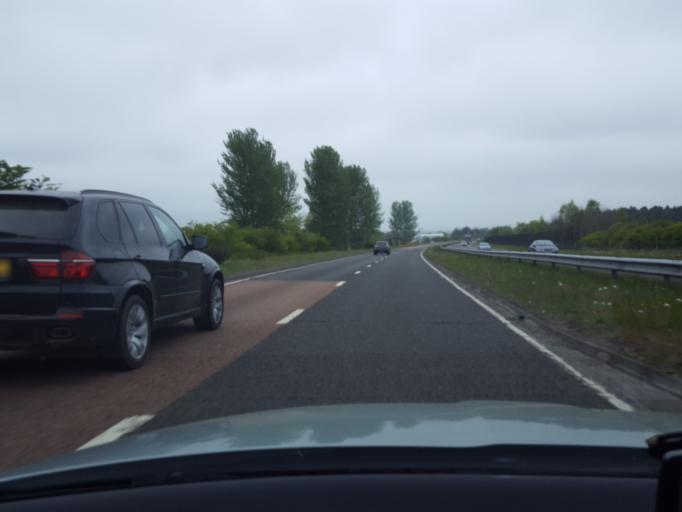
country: GB
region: Scotland
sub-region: Angus
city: Forfar
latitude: 56.6379
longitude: -2.9254
